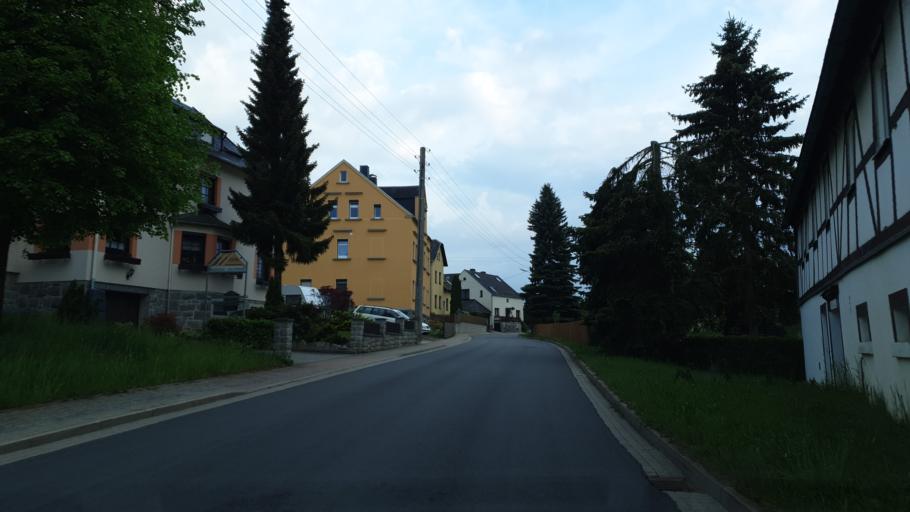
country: DE
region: Saxony
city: Lugau
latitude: 50.7147
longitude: 12.7438
